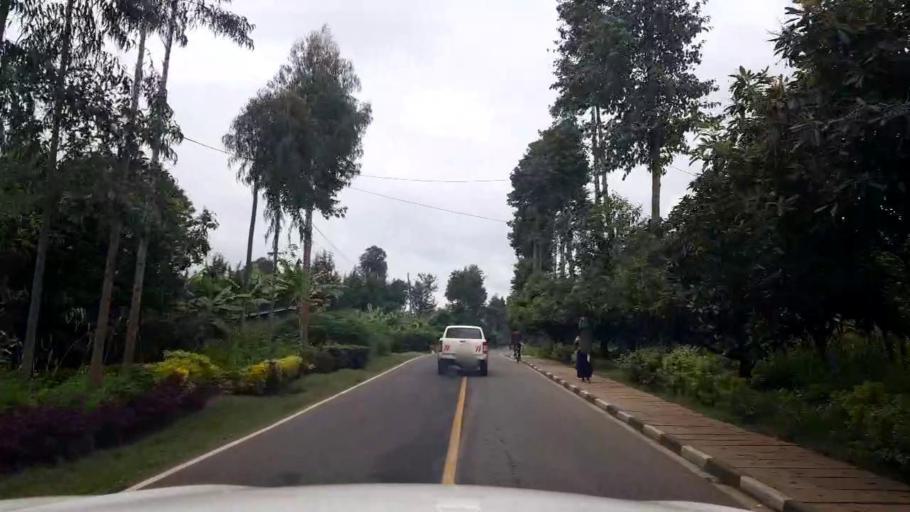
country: RW
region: Northern Province
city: Musanze
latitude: -1.4535
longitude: 29.6007
